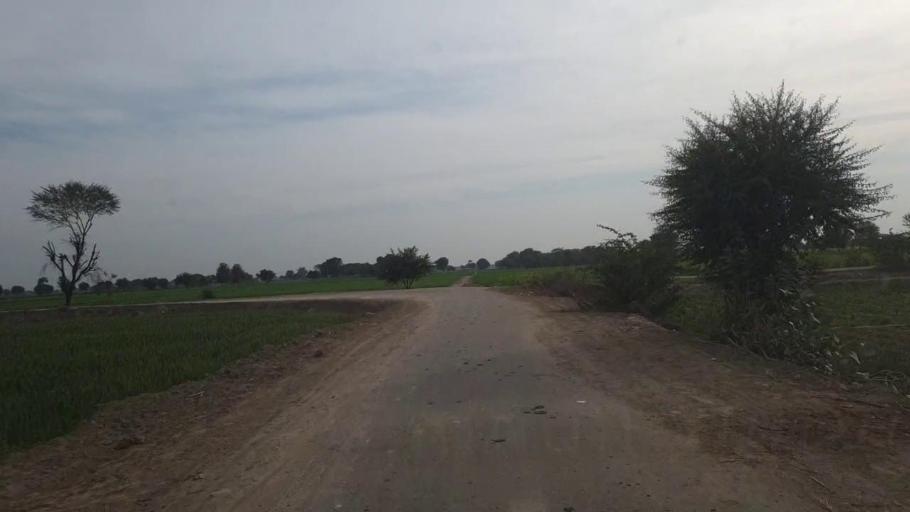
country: PK
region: Sindh
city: Shahpur Chakar
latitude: 26.1027
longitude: 68.5232
